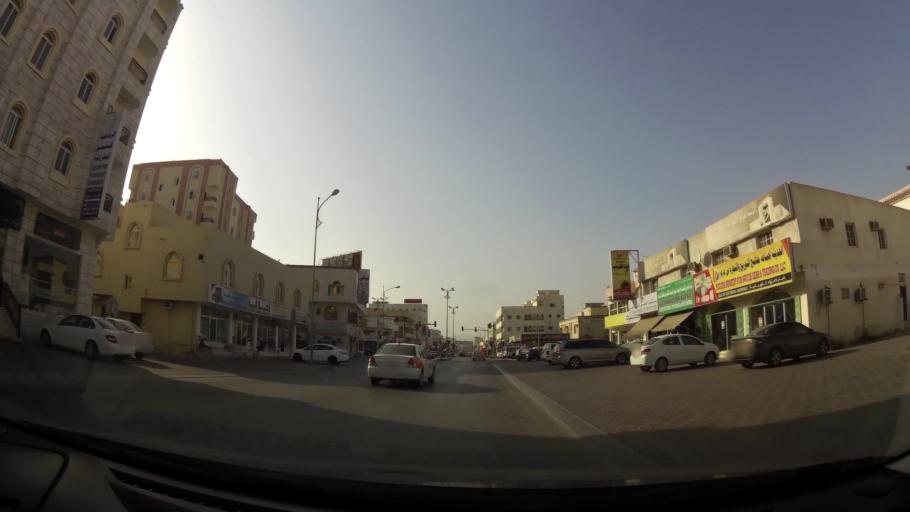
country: OM
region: Zufar
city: Salalah
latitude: 17.0123
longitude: 54.0860
